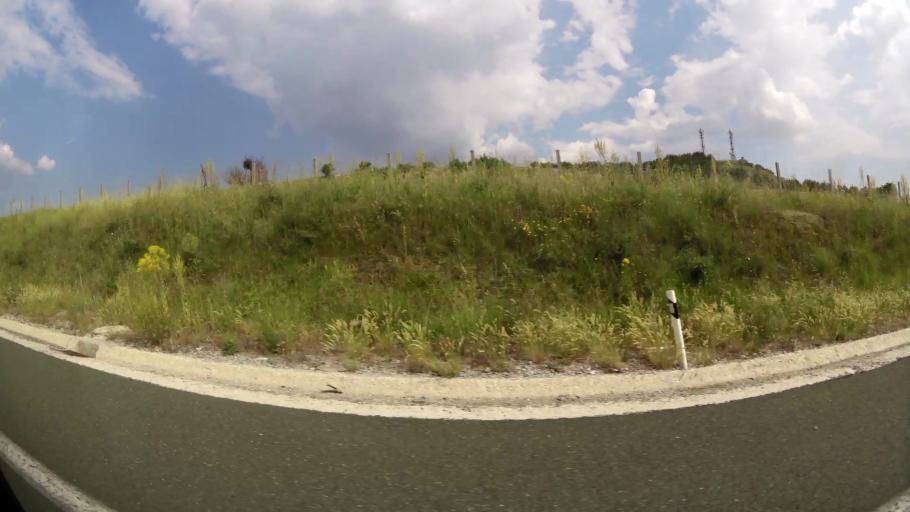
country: GR
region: West Macedonia
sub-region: Nomos Kozanis
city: Koila
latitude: 40.3605
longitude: 21.8179
